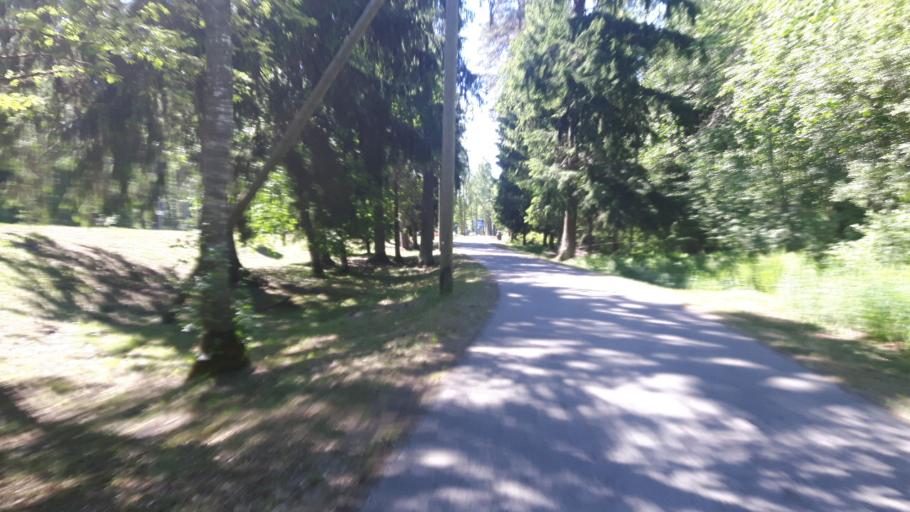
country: EE
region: Harju
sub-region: Saku vald
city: Saku
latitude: 59.3099
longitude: 24.6784
